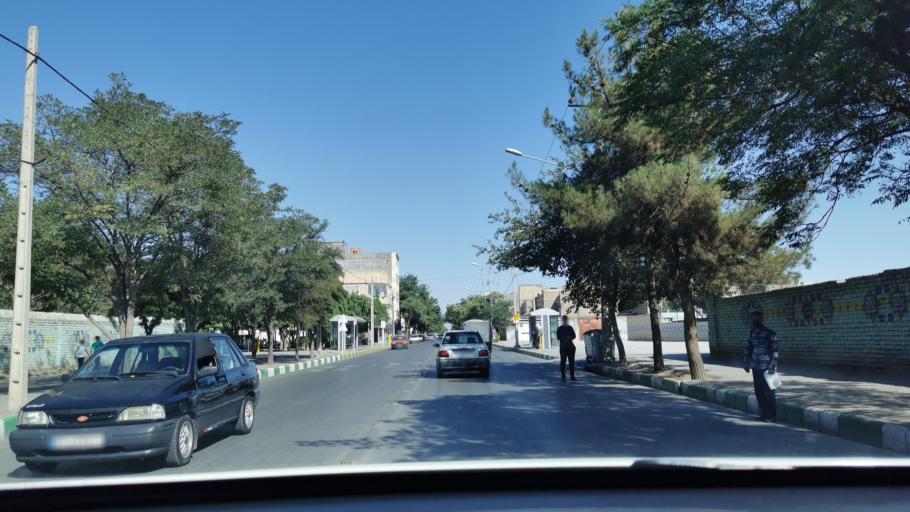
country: IR
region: Razavi Khorasan
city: Mashhad
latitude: 36.3344
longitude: 59.6390
